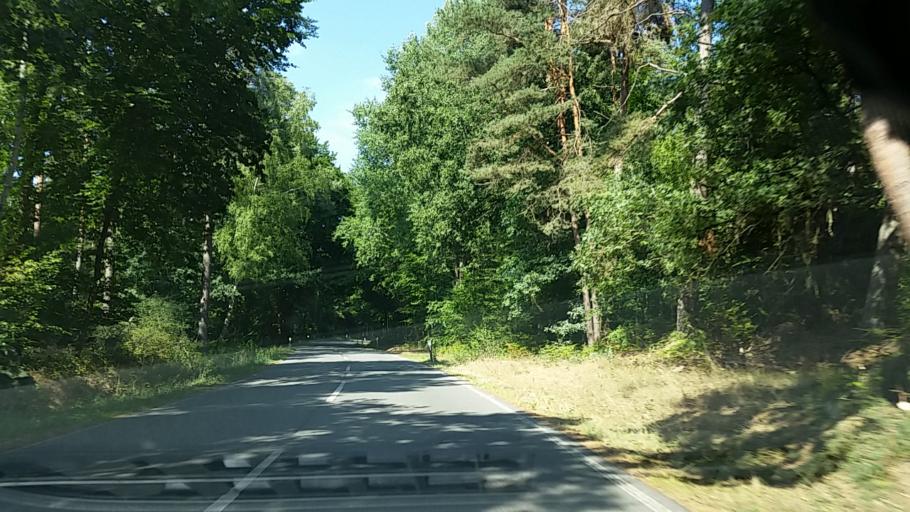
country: DE
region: Lower Saxony
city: Jelmstorf
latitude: 53.1154
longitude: 10.5463
